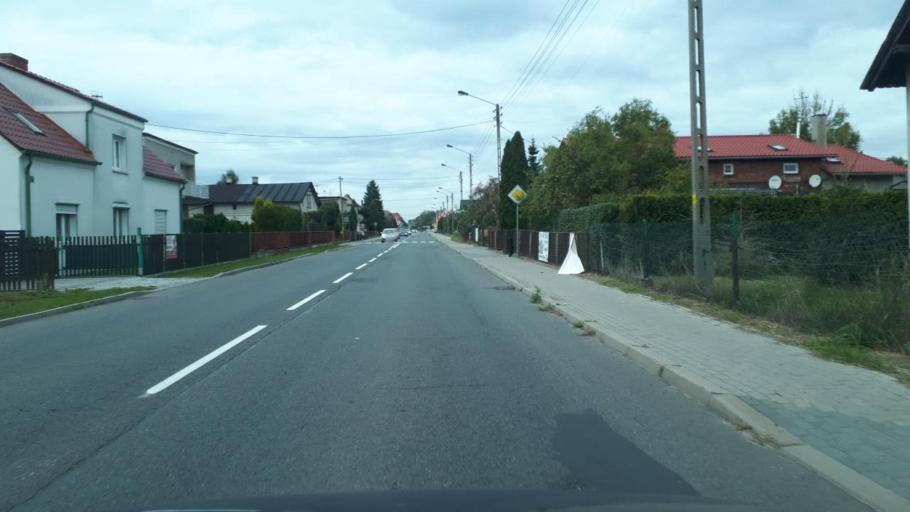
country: PL
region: Opole Voivodeship
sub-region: Powiat strzelecki
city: Zawadzkie
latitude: 50.6010
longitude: 18.4902
